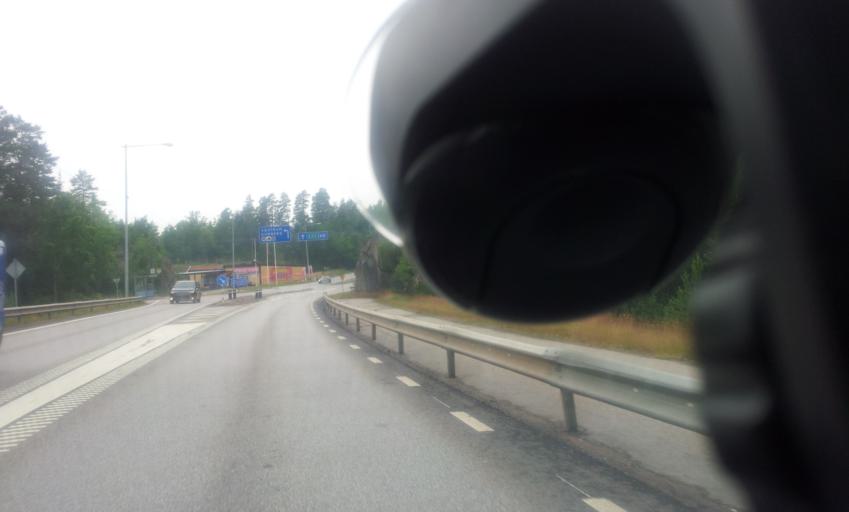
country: SE
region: Kalmar
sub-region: Vasterviks Kommun
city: Vaestervik
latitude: 57.7268
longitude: 16.5178
